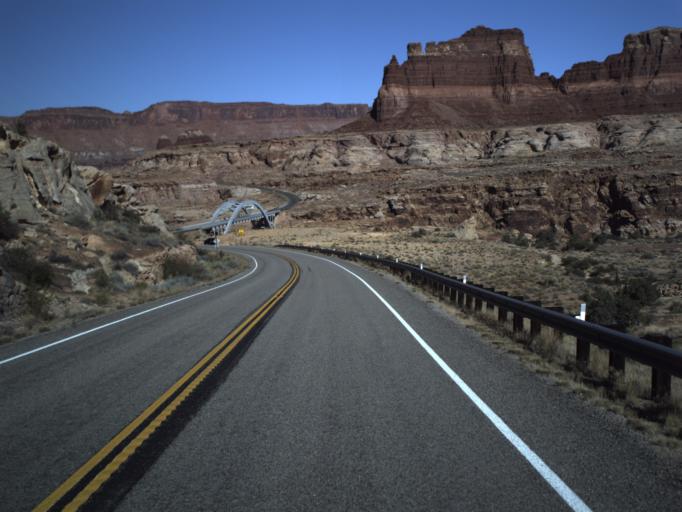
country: US
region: Utah
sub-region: San Juan County
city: Blanding
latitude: 37.8872
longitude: -110.3664
